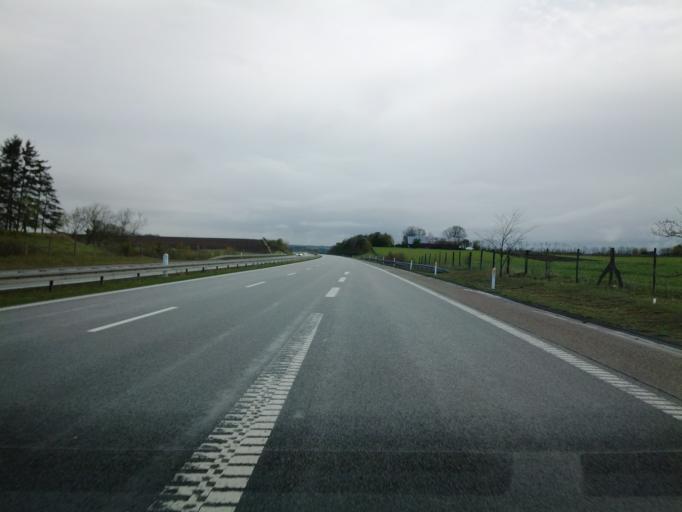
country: DK
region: North Denmark
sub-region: Bronderslev Kommune
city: Hjallerup
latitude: 57.1731
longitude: 10.1936
